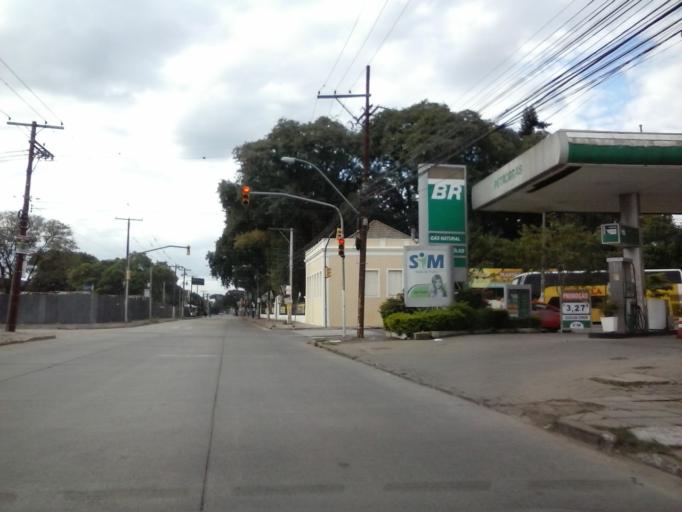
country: BR
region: Rio Grande do Sul
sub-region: Porto Alegre
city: Porto Alegre
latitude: -30.0084
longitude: -51.2094
